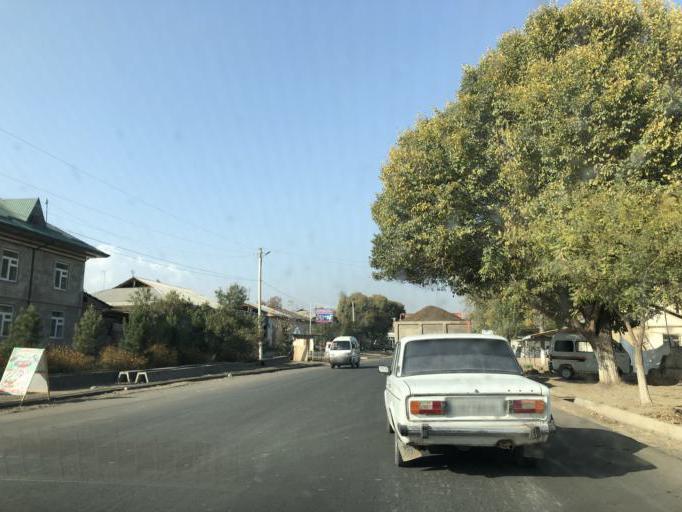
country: UZ
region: Namangan
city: Chust Shahri
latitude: 41.0719
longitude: 71.2045
